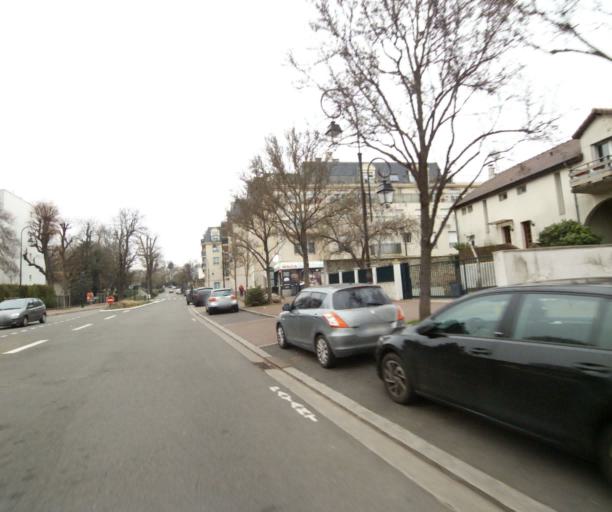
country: FR
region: Ile-de-France
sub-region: Departement des Hauts-de-Seine
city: Saint-Cloud
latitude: 48.8421
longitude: 2.1992
